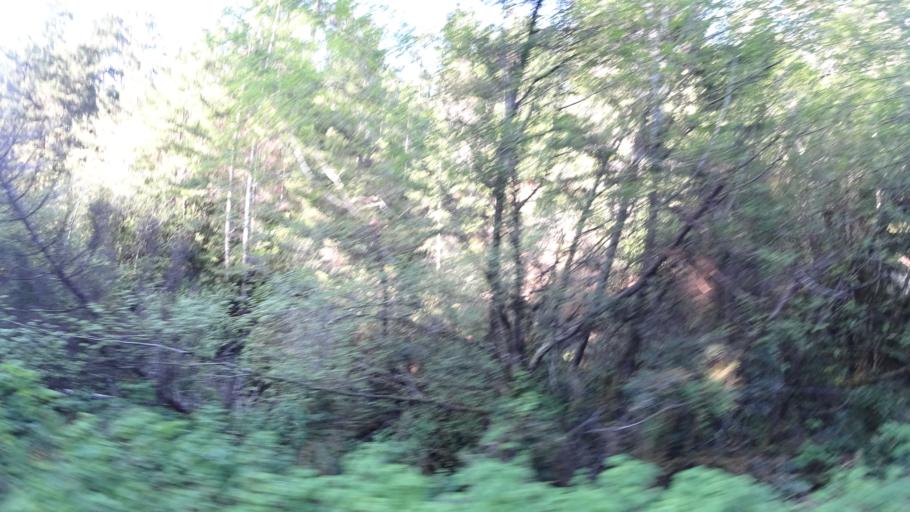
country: US
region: Oregon
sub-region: Douglas County
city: Reedsport
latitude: 43.7474
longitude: -124.1745
